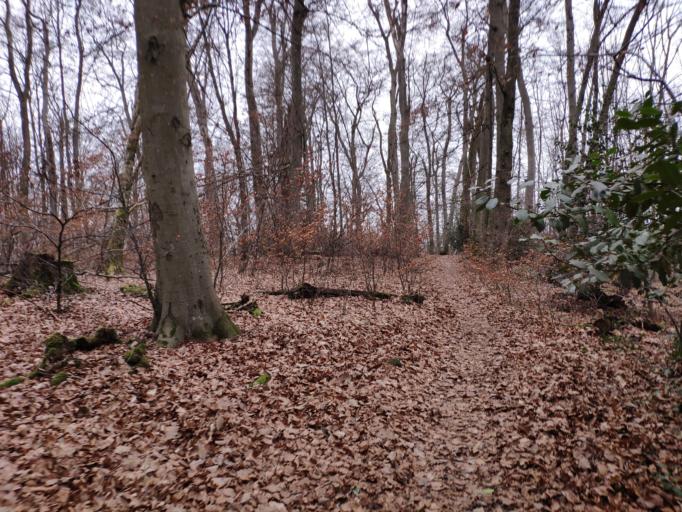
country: DE
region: Baden-Wuerttemberg
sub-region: Freiburg Region
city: Inzlingen
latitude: 47.5822
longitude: 7.6810
